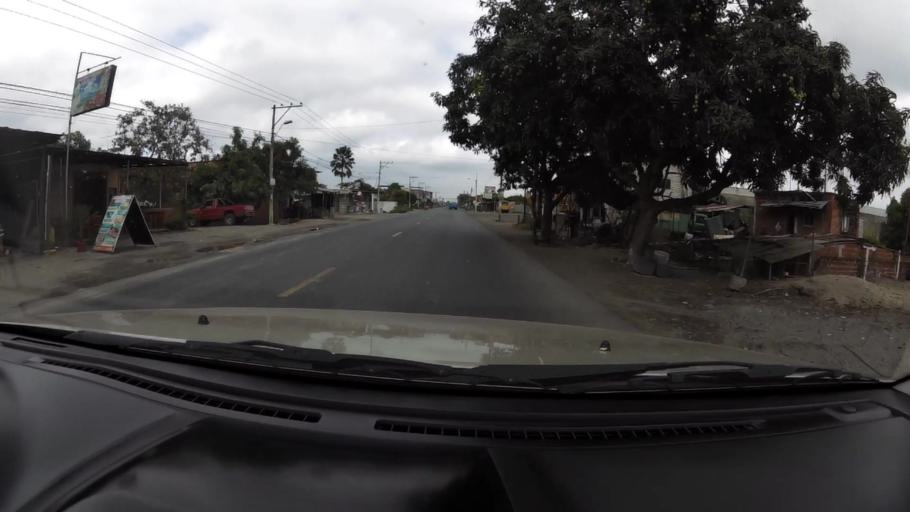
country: EC
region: Guayas
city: Naranjal
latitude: -2.6839
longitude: -79.6259
